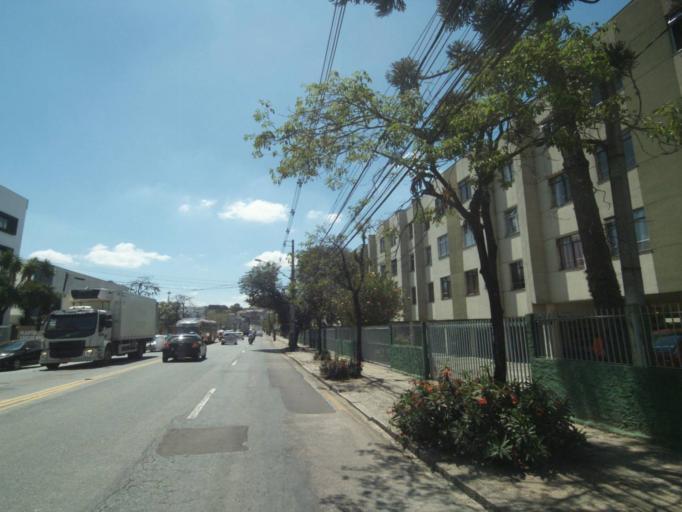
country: BR
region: Parana
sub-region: Curitiba
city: Curitiba
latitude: -25.3928
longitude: -49.2268
